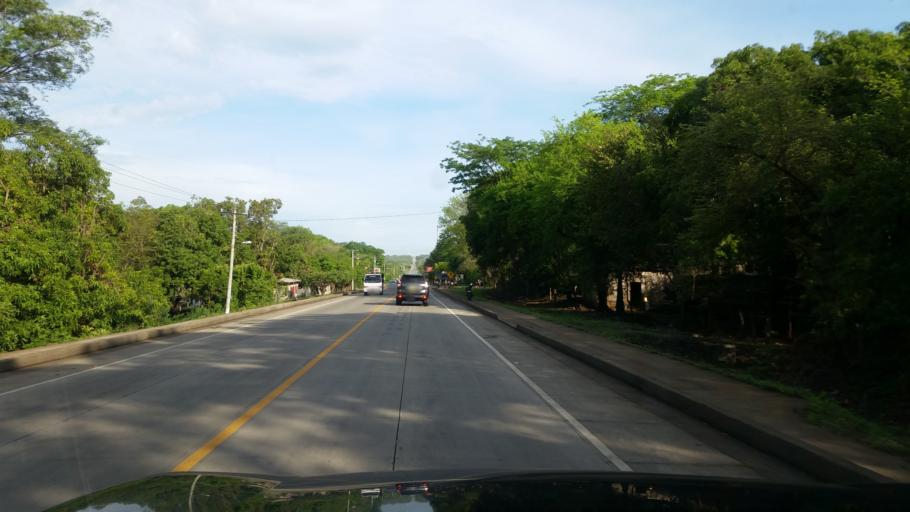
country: NI
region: Managua
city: Carlos Fonseca Amador
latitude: 12.1083
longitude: -86.5923
